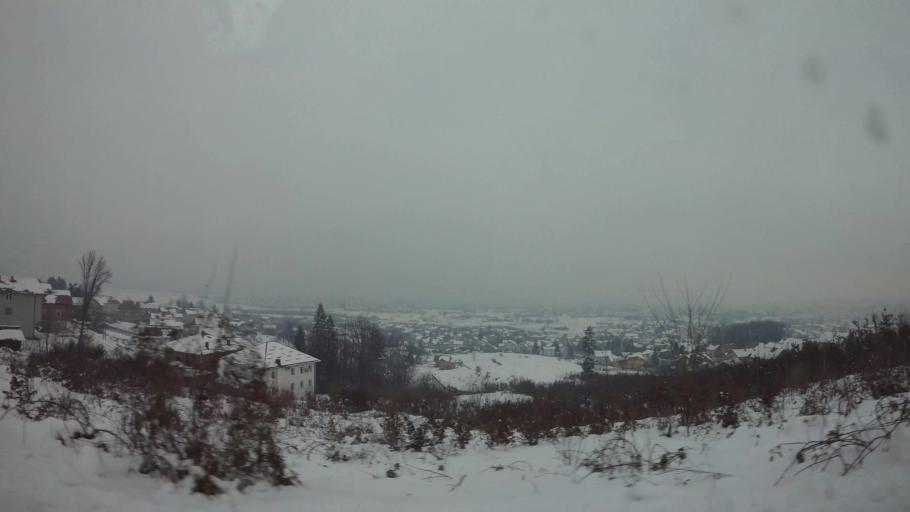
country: BA
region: Federation of Bosnia and Herzegovina
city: Hadzici
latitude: 43.8481
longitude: 18.2714
